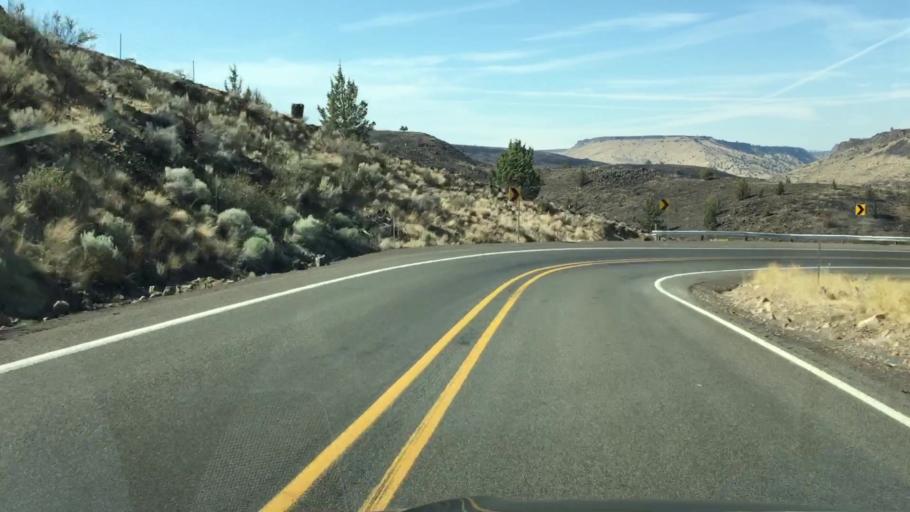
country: US
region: Oregon
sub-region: Wasco County
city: The Dalles
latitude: 45.1652
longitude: -121.0866
